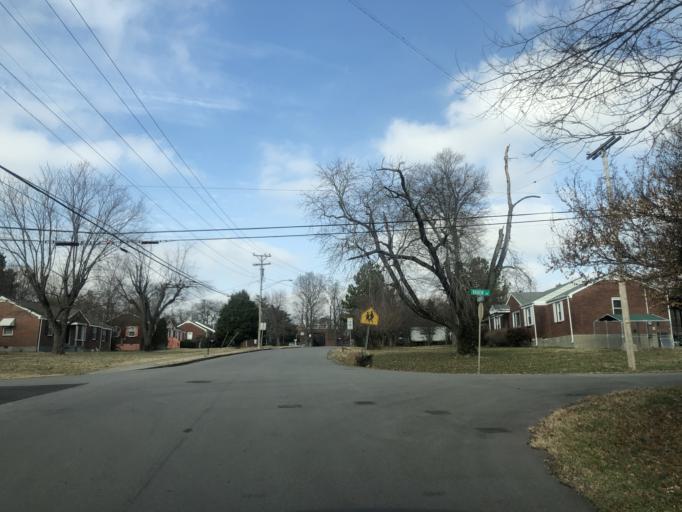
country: US
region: Tennessee
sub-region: Davidson County
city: Oak Hill
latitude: 36.0999
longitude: -86.7215
